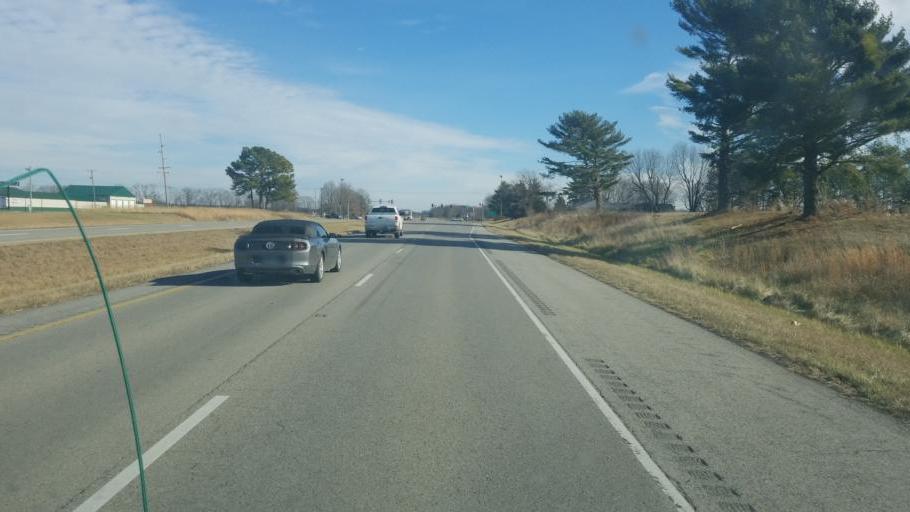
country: US
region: Illinois
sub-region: Williamson County
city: Marion
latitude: 37.7291
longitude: -88.8581
